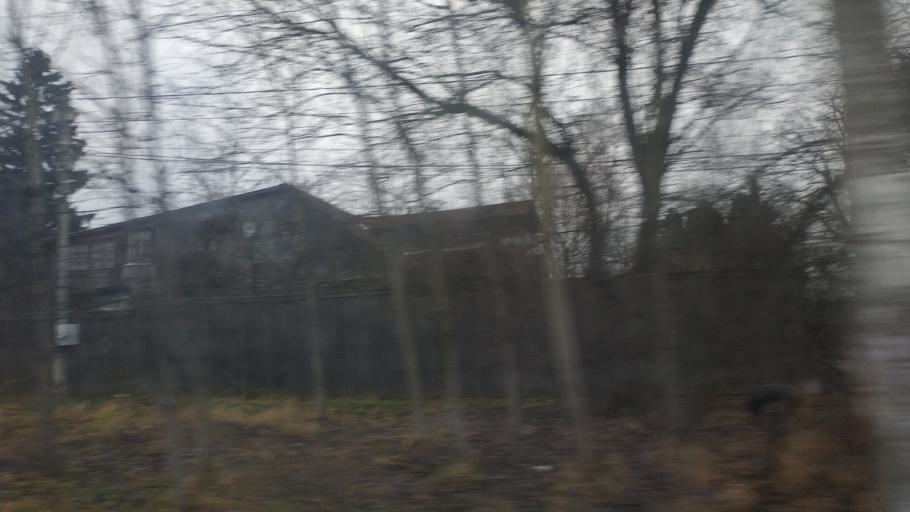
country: RU
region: Moskovskaya
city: Lugovaya
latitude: 56.0538
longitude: 37.4782
